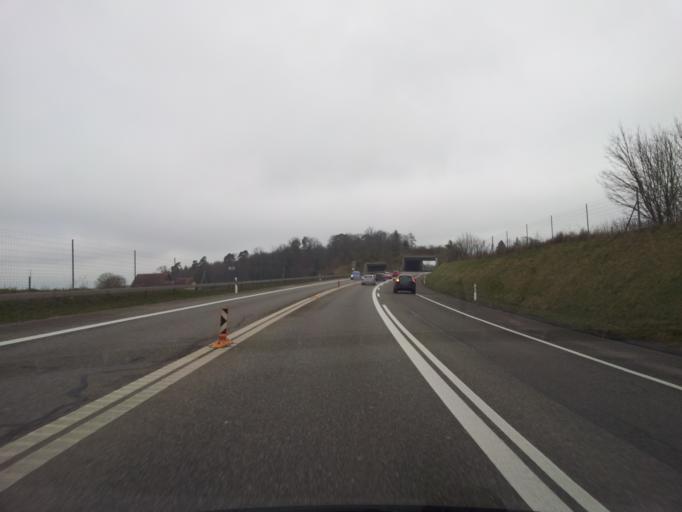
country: CH
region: Zurich
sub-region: Bezirk Andelfingen
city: Henggart
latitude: 47.5757
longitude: 8.6837
